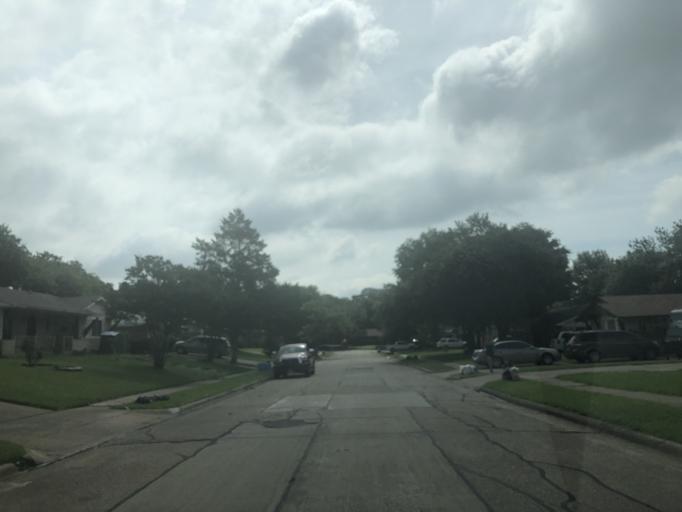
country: US
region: Texas
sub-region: Dallas County
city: Irving
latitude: 32.7991
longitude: -96.9705
